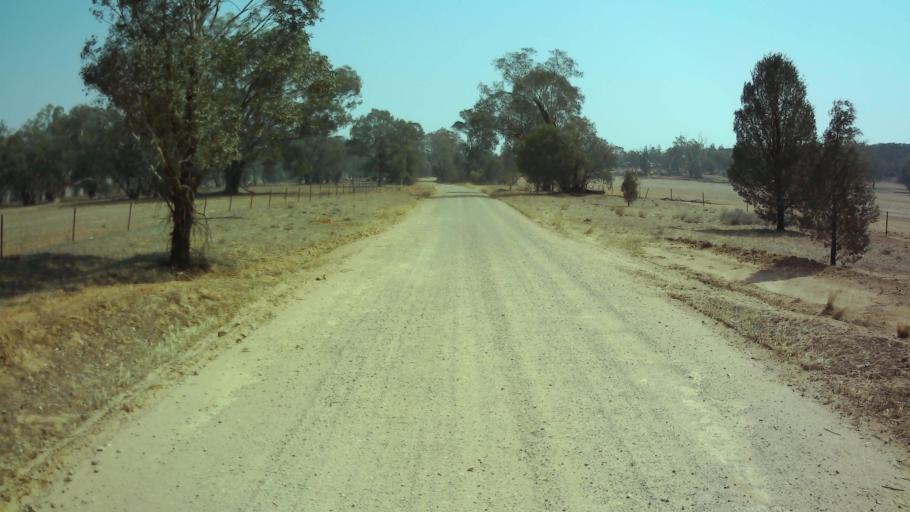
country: AU
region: New South Wales
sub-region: Weddin
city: Grenfell
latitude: -33.6679
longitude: 148.2747
